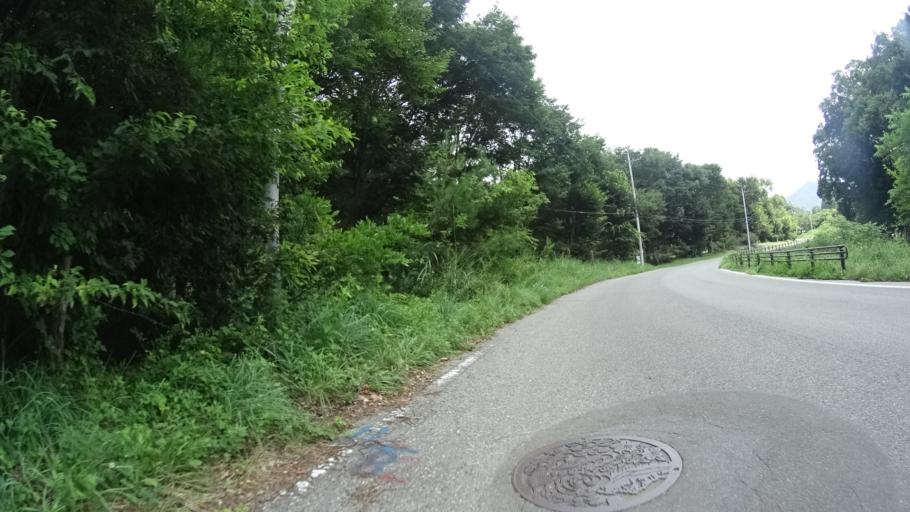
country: JP
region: Yamanashi
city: Nirasaki
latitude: 35.8838
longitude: 138.5236
